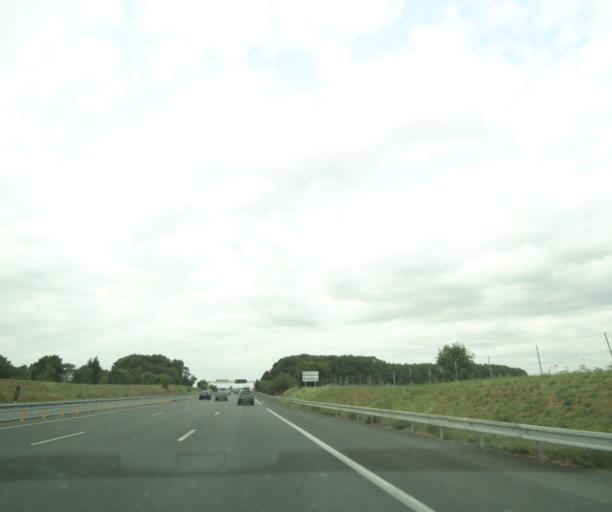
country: FR
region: Centre
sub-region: Departement d'Indre-et-Loire
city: Rochecorbon
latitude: 47.4147
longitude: 0.7298
